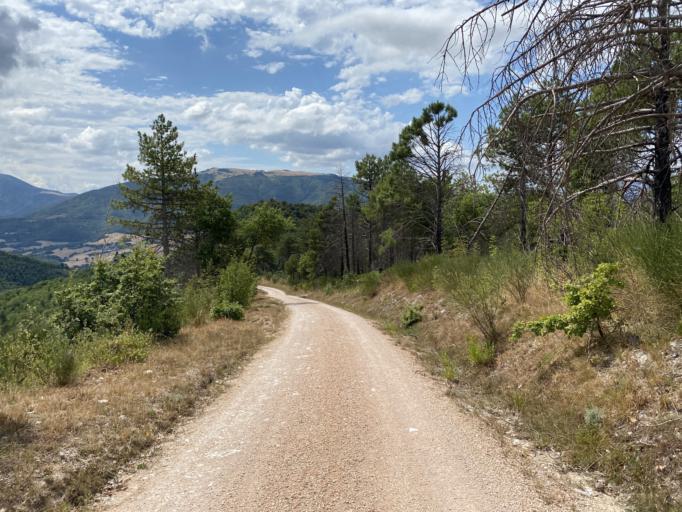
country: IT
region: The Marches
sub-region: Provincia di Pesaro e Urbino
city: Canavaccio
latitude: 43.7076
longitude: 12.7150
